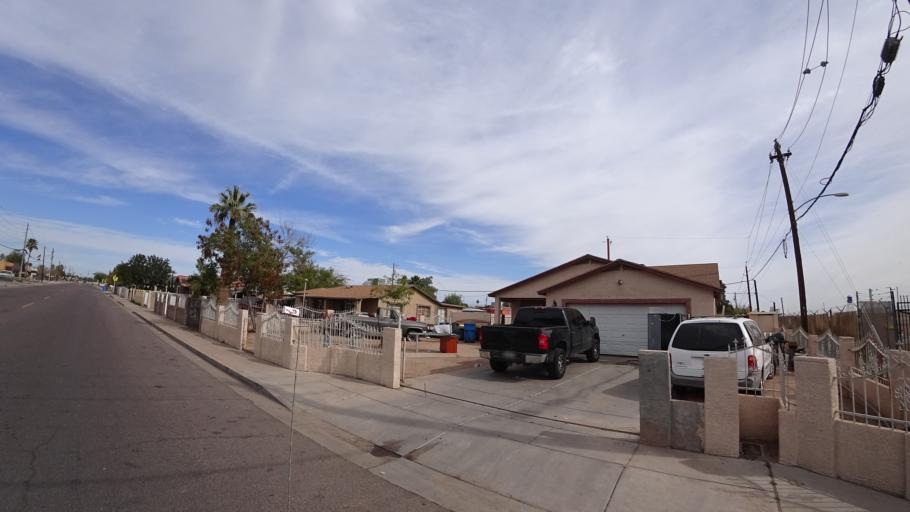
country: US
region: Arizona
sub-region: Maricopa County
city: Phoenix
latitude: 33.4461
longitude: -112.1260
